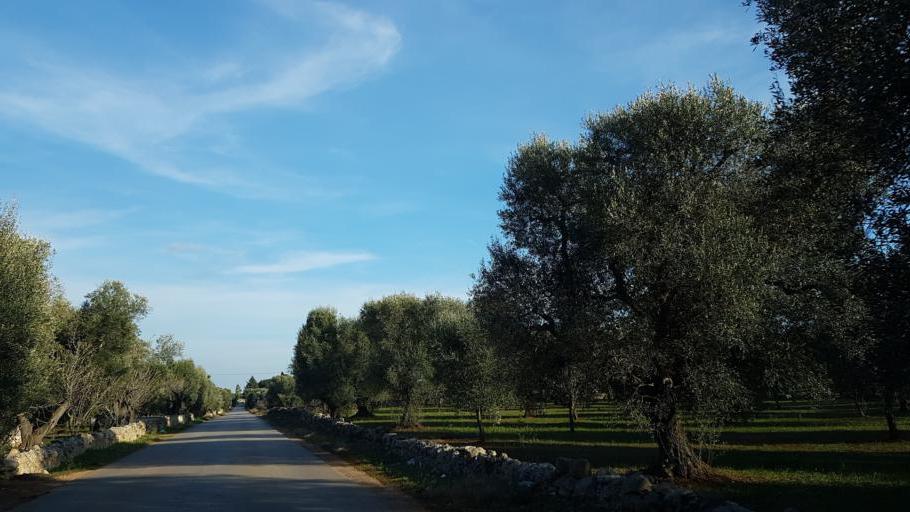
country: IT
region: Apulia
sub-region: Provincia di Brindisi
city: San Vito dei Normanni
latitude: 40.7054
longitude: 17.7082
